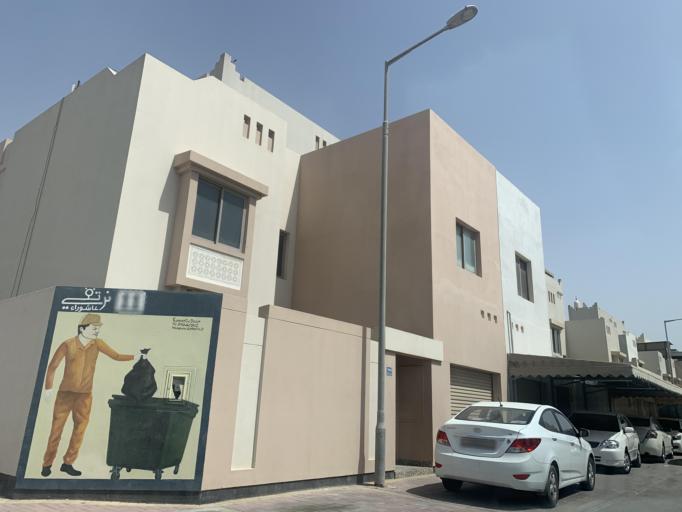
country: BH
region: Central Governorate
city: Madinat Hamad
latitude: 26.1478
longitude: 50.4974
